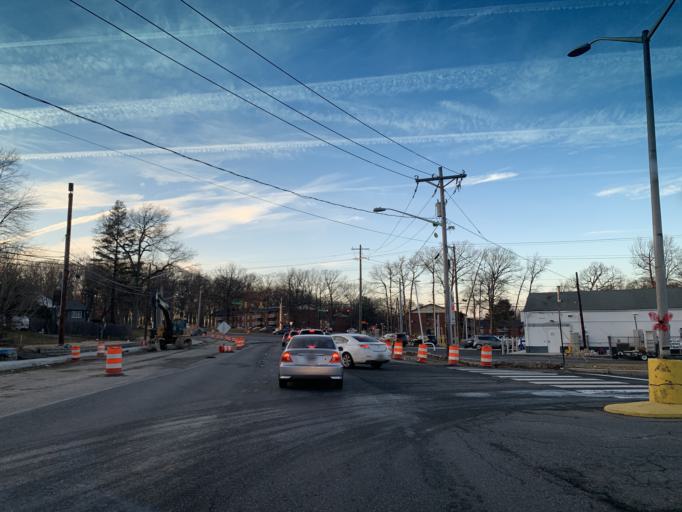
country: US
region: Delaware
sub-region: New Castle County
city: Bear
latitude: 39.6618
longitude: -75.6413
